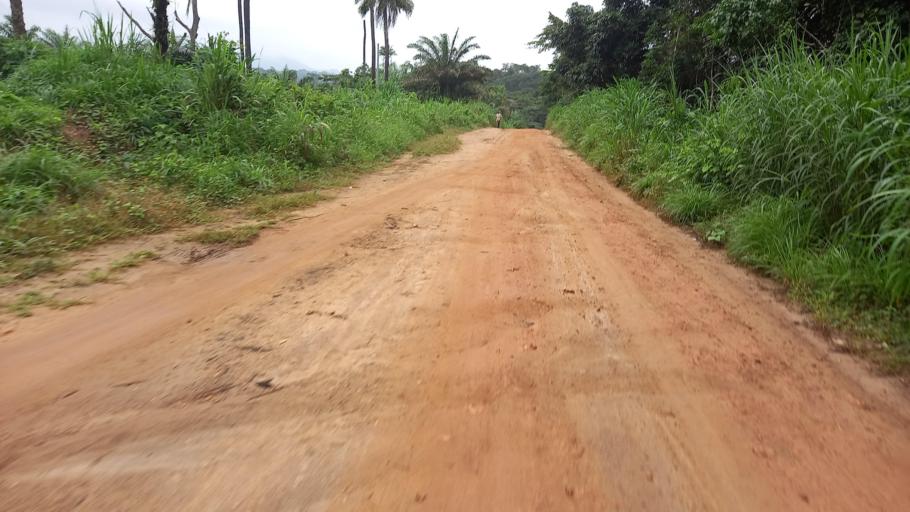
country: SL
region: Eastern Province
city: Kailahun
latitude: 8.2541
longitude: -10.5291
